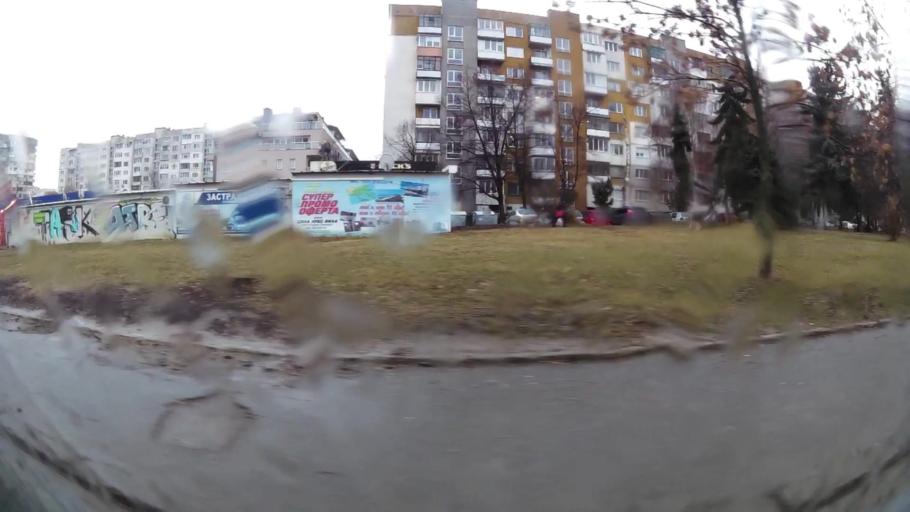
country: BG
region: Sofia-Capital
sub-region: Stolichna Obshtina
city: Sofia
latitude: 42.6649
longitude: 23.3613
